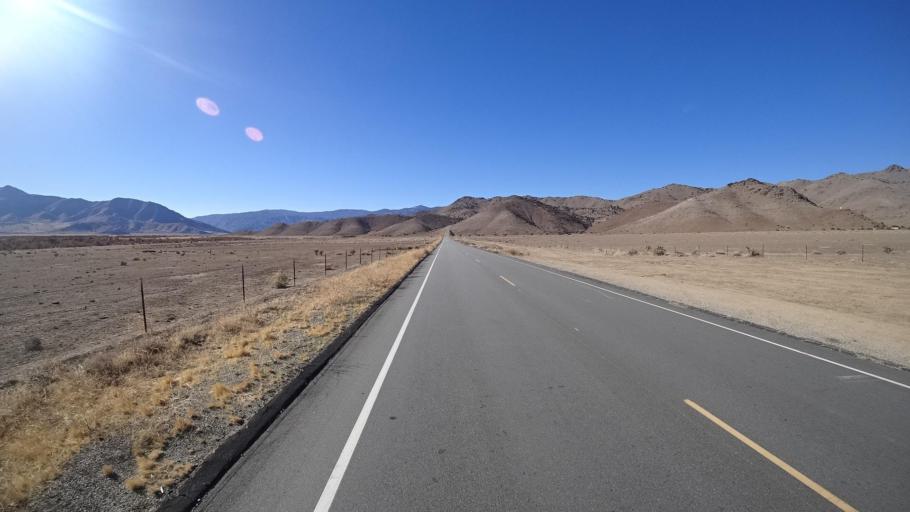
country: US
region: California
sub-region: Kern County
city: Weldon
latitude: 35.6795
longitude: -118.3671
